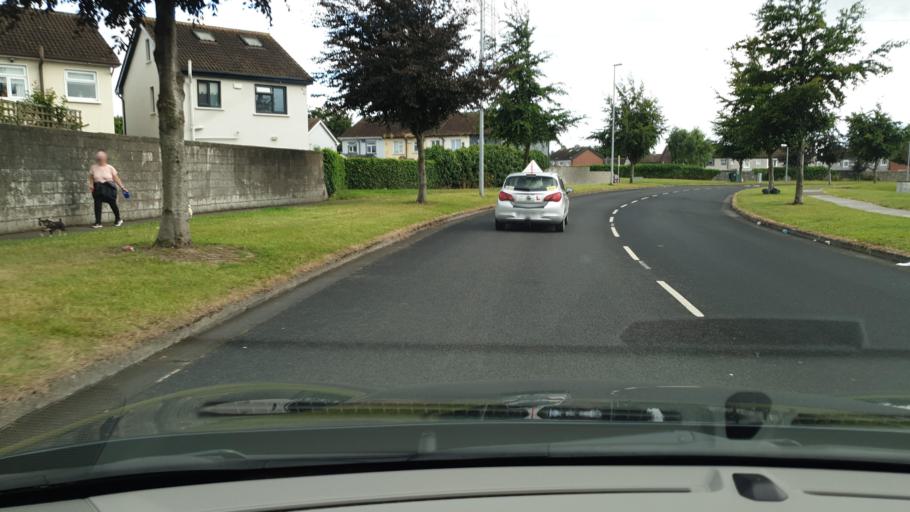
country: IE
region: Leinster
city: Clondalkin
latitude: 53.3381
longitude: -6.3943
